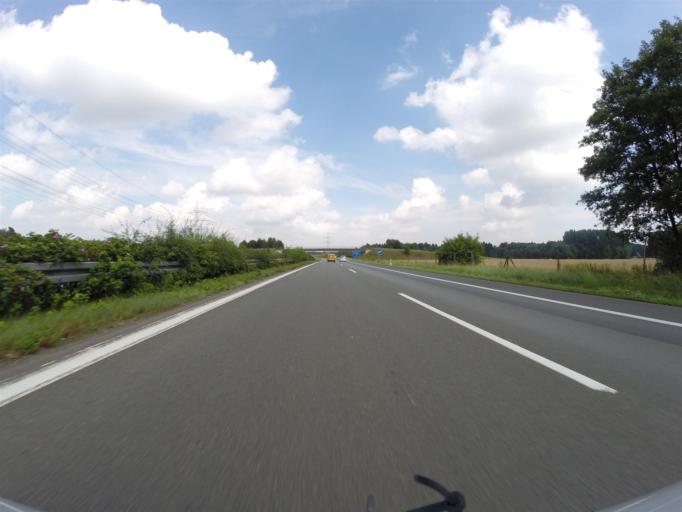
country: DE
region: North Rhine-Westphalia
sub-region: Regierungsbezirk Detmold
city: Oerlinghausen
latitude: 51.9129
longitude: 8.6192
